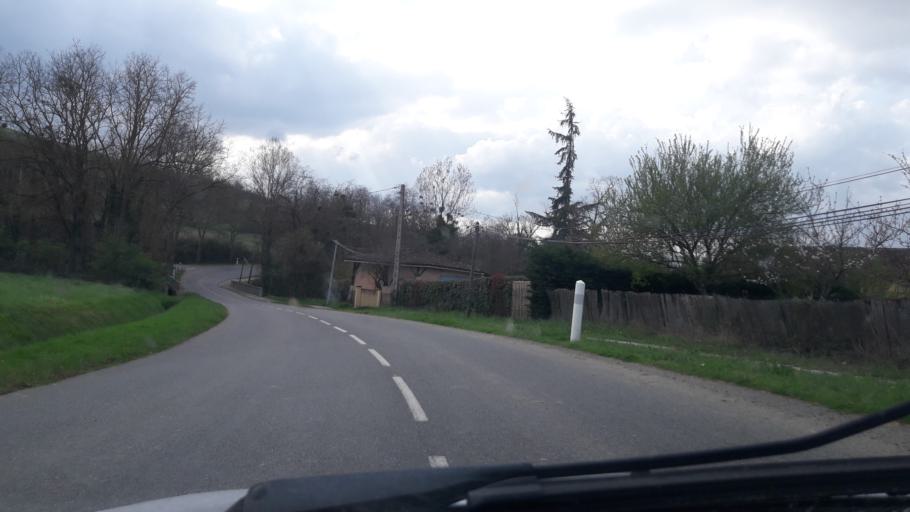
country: FR
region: Midi-Pyrenees
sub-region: Departement de la Haute-Garonne
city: Rieux-Volvestre
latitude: 43.2629
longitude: 1.2195
